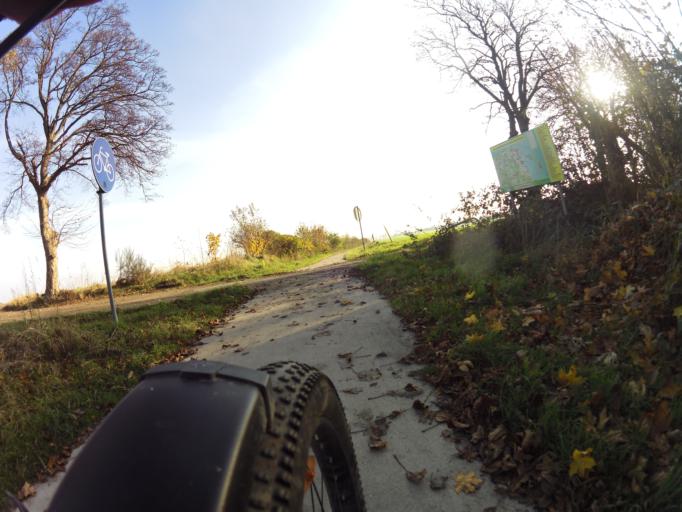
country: PL
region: Pomeranian Voivodeship
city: Strzelno
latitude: 54.7653
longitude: 18.2497
